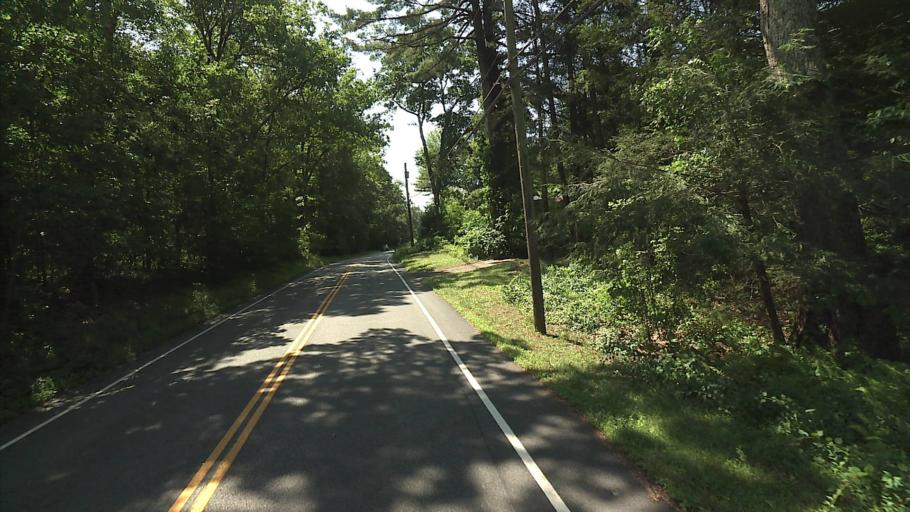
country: US
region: Connecticut
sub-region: Litchfield County
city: West Torrington
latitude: 41.8347
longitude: -73.1516
